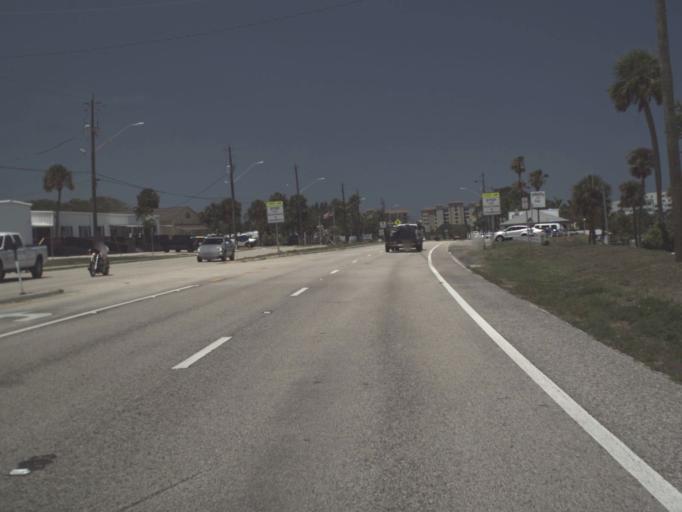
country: US
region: Florida
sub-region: Brevard County
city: Malabar
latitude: 28.0107
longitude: -80.5671
